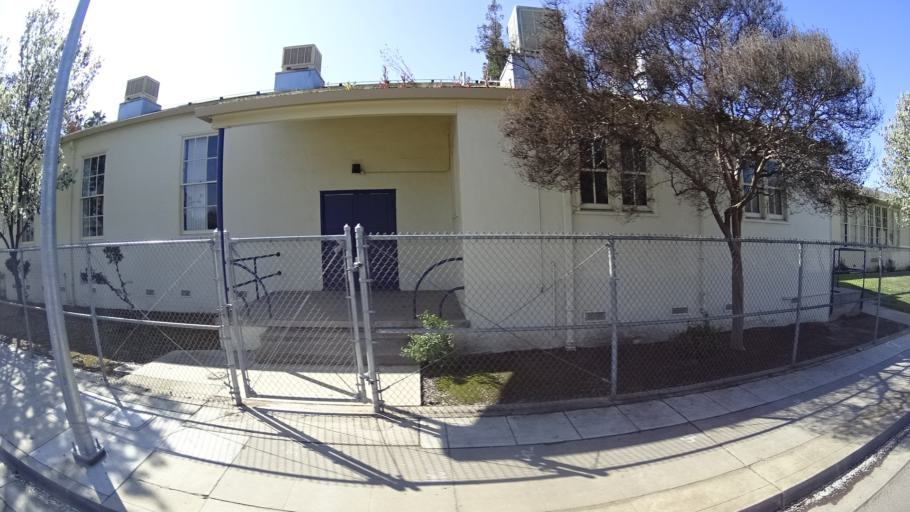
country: US
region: California
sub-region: Fresno County
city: Fresno
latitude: 36.7794
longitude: -119.8114
